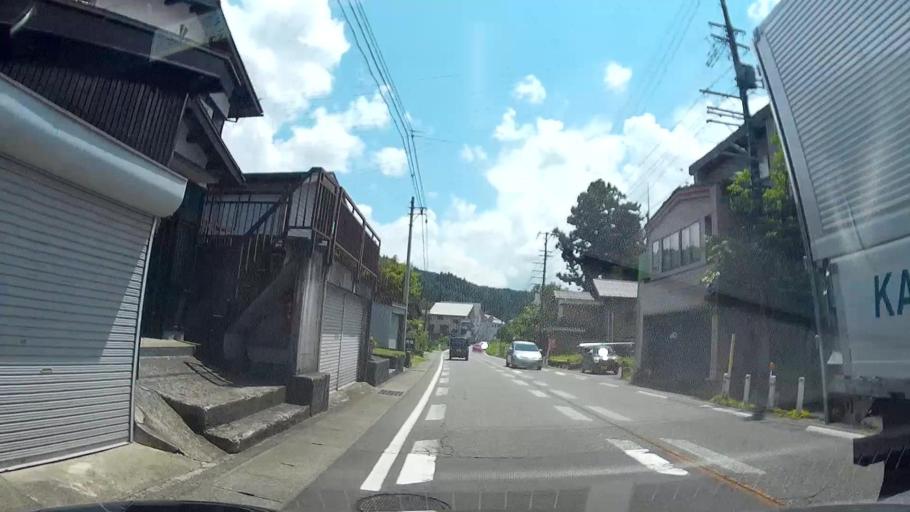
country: JP
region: Niigata
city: Tokamachi
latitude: 37.0733
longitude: 138.7152
